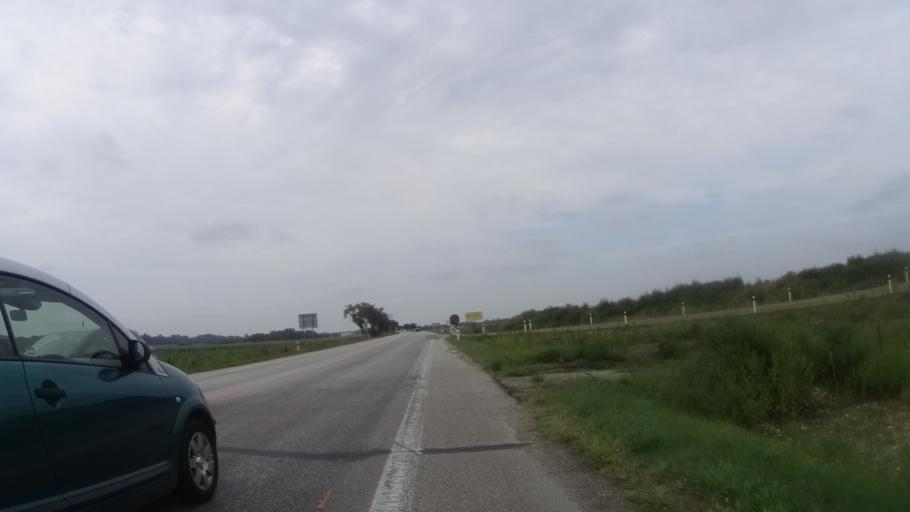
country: SK
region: Nitriansky
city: Komarno
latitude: 47.7657
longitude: 18.0843
